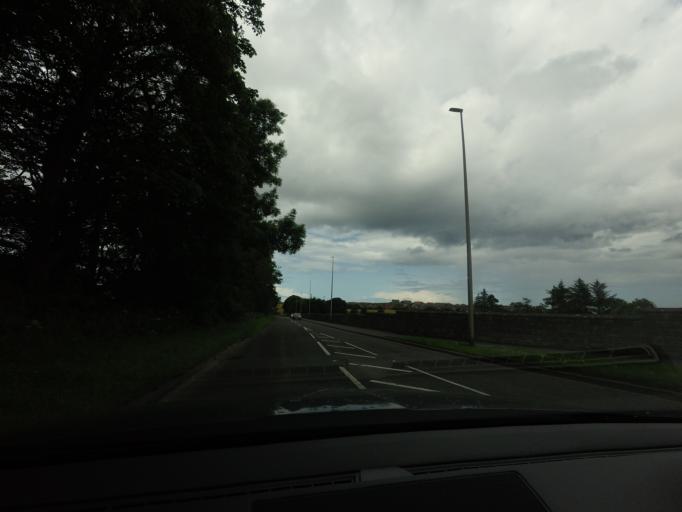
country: GB
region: Scotland
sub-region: Aberdeenshire
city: Macduff
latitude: 57.6590
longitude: -2.4903
